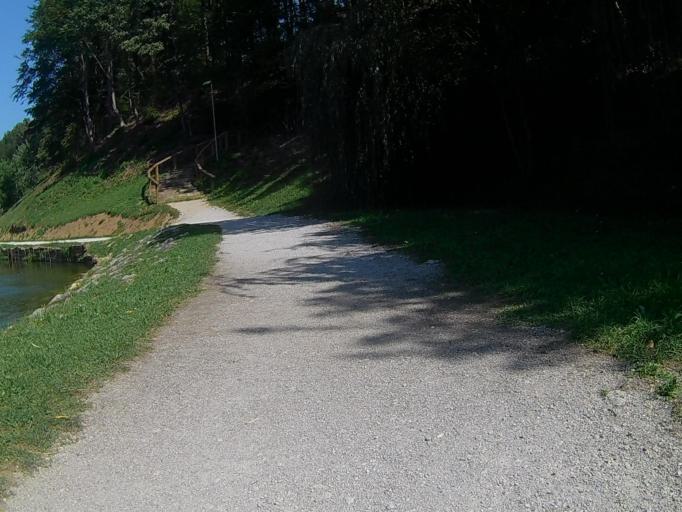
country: SI
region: Zrece
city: Zrece
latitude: 46.3682
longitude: 15.3858
